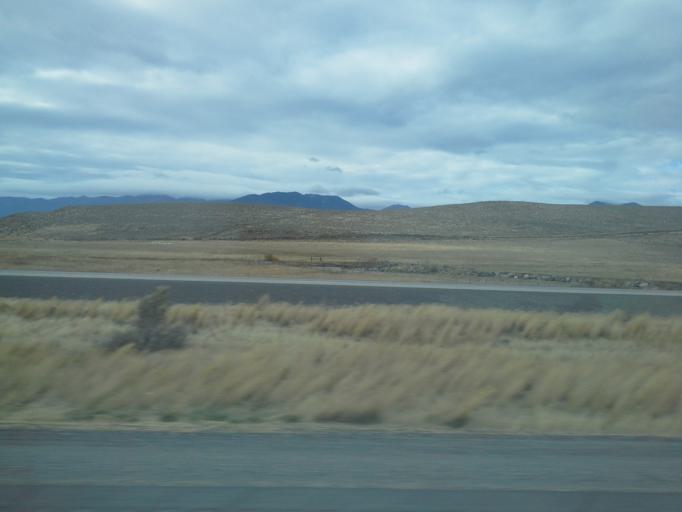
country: US
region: Oregon
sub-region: Baker County
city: Baker City
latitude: 44.9764
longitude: -117.8841
